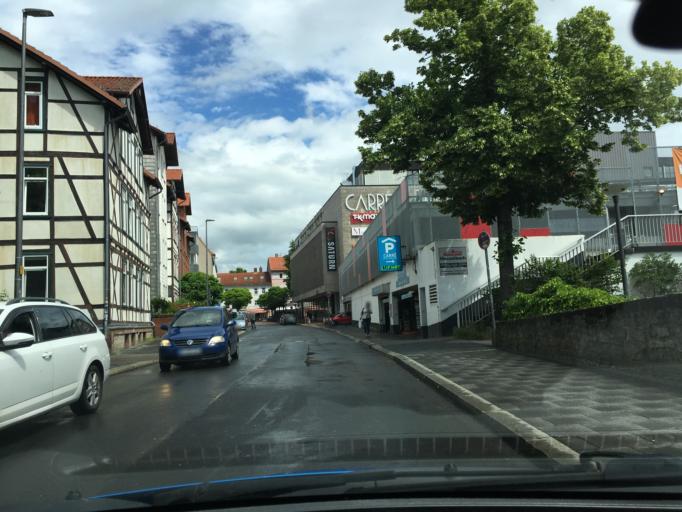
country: DE
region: Lower Saxony
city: Goettingen
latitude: 51.5366
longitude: 9.9326
